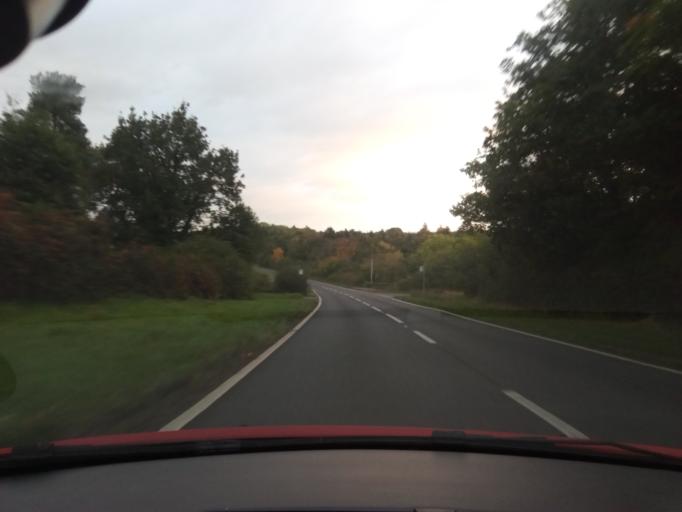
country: GB
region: England
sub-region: Essex
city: Rowhedge
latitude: 51.8448
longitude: 0.9175
